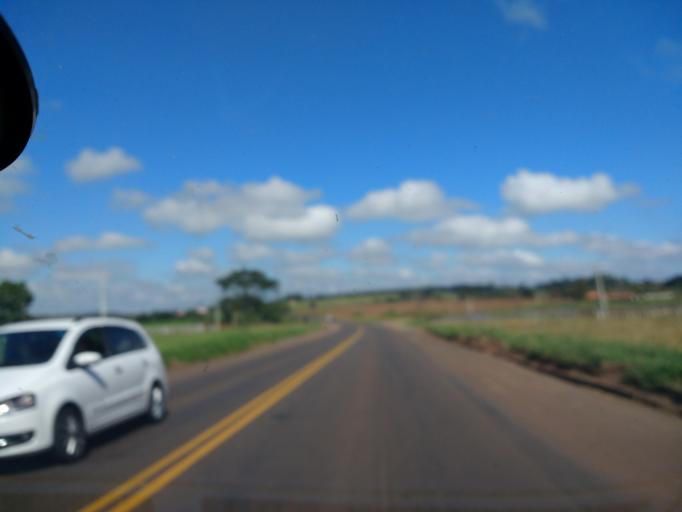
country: BR
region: Parana
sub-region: Cianorte
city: Cianorte
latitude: -23.6941
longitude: -52.6390
